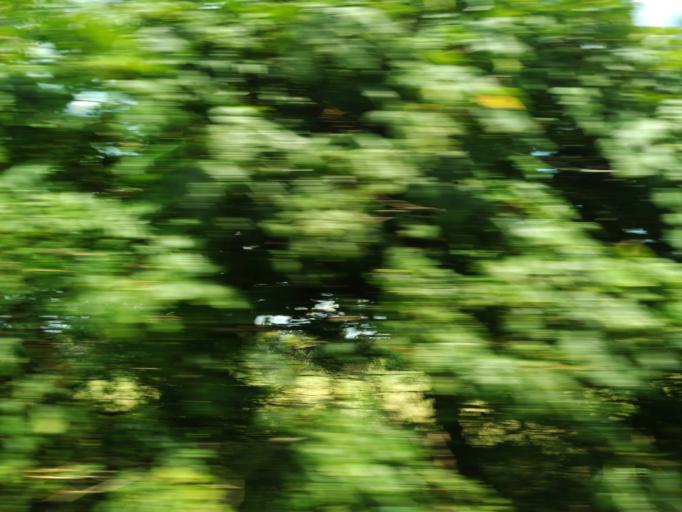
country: US
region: Maryland
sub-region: Anne Arundel County
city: Deale
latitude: 38.8151
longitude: -76.5781
